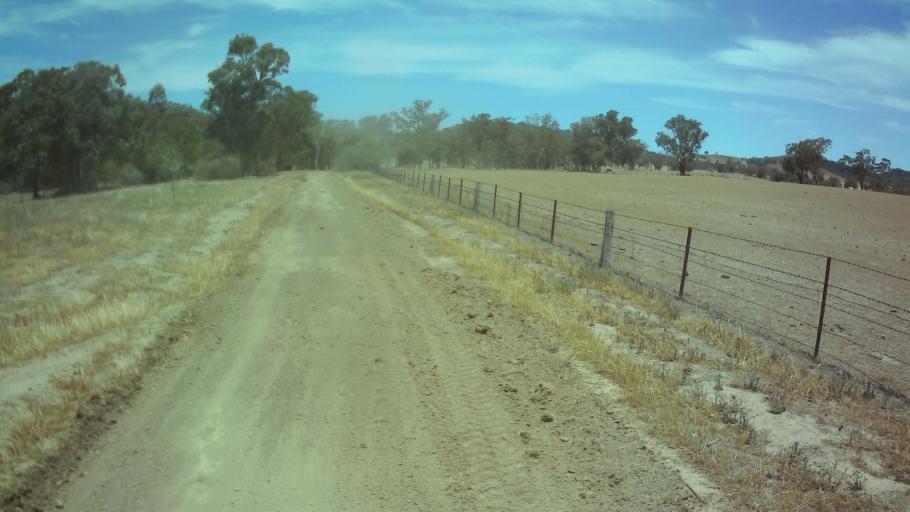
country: AU
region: New South Wales
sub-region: Weddin
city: Grenfell
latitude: -33.7658
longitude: 148.1490
